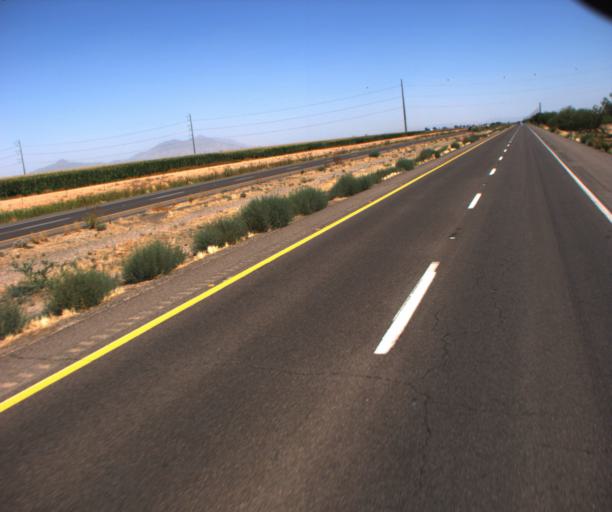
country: US
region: Arizona
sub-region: Pinal County
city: Maricopa
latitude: 32.9578
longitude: -112.0477
